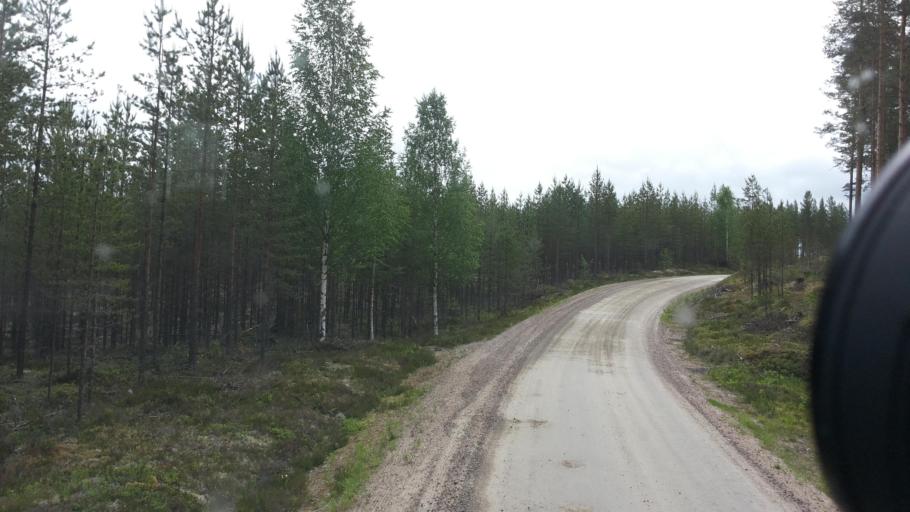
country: SE
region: Gaevleborg
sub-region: Ovanakers Kommun
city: Edsbyn
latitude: 61.5087
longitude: 15.3400
